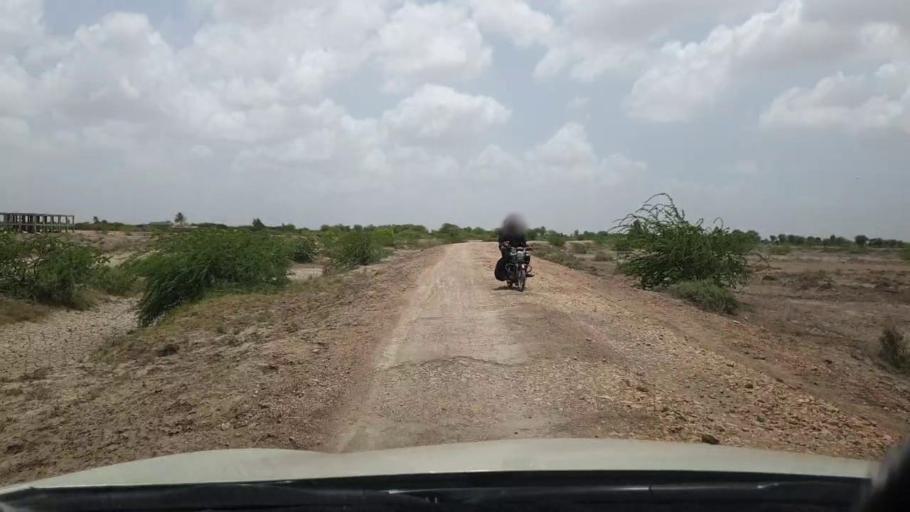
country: PK
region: Sindh
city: Kadhan
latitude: 24.3796
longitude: 68.9296
